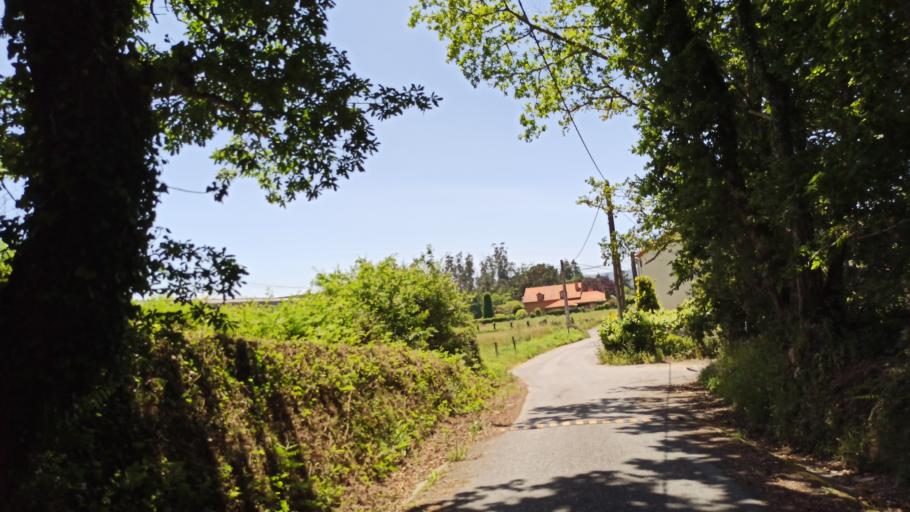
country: ES
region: Galicia
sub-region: Provincia da Coruna
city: Negreira
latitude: 42.9121
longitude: -8.7247
